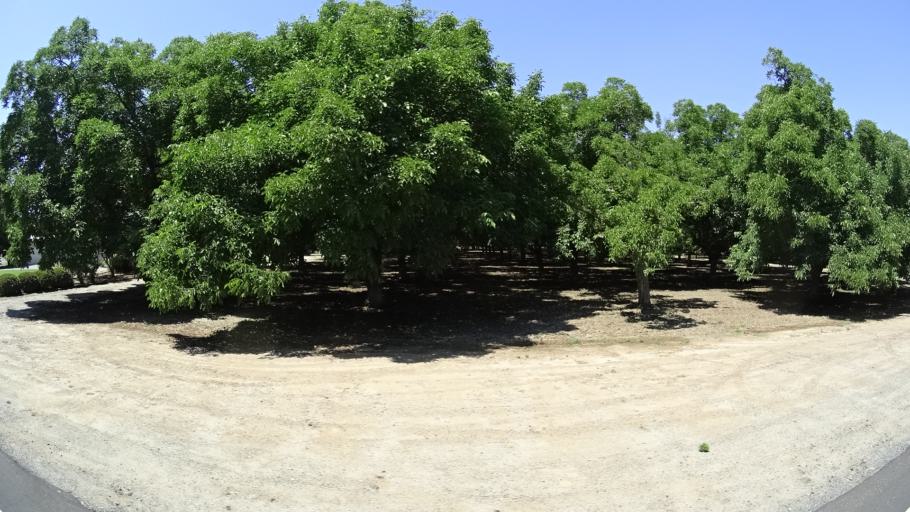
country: US
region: California
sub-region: Kings County
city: Lucerne
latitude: 36.3698
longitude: -119.6731
